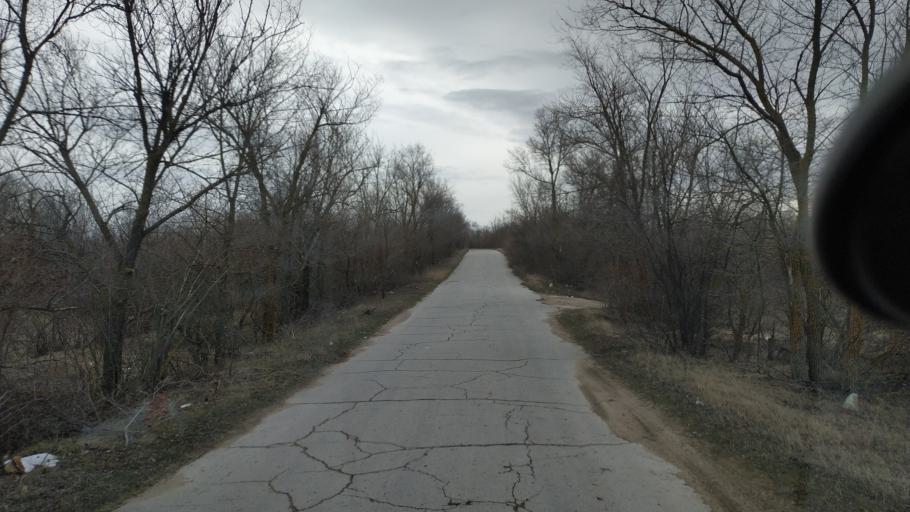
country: MD
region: Telenesti
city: Cocieri
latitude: 47.3306
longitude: 29.0891
